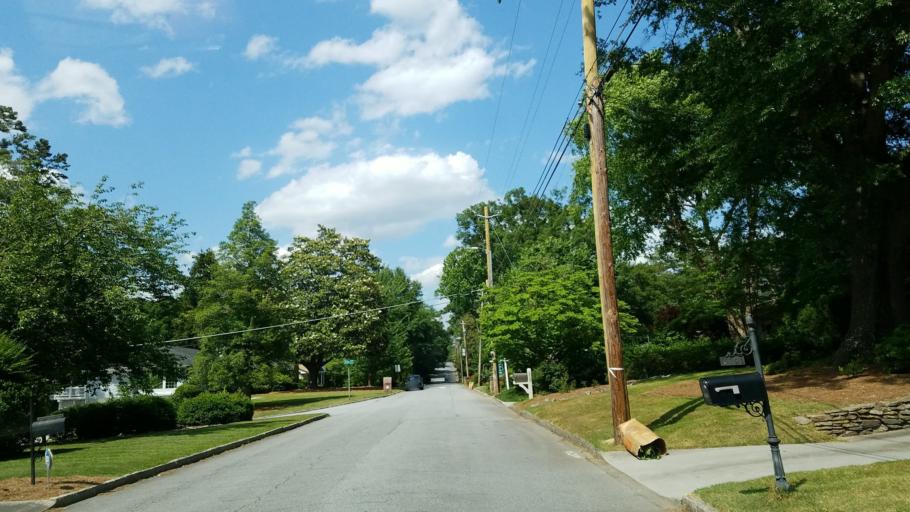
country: US
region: Georgia
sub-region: DeKalb County
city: North Atlanta
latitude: 33.8252
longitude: -84.3723
